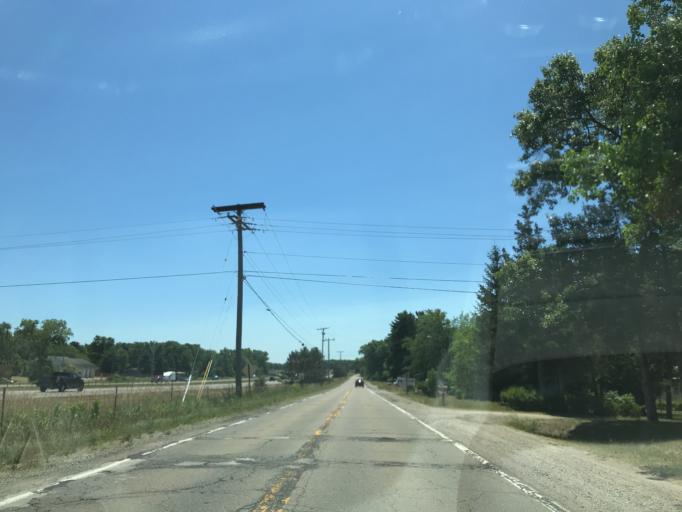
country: US
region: Michigan
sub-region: Livingston County
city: Whitmore Lake
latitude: 42.4762
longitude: -83.7559
